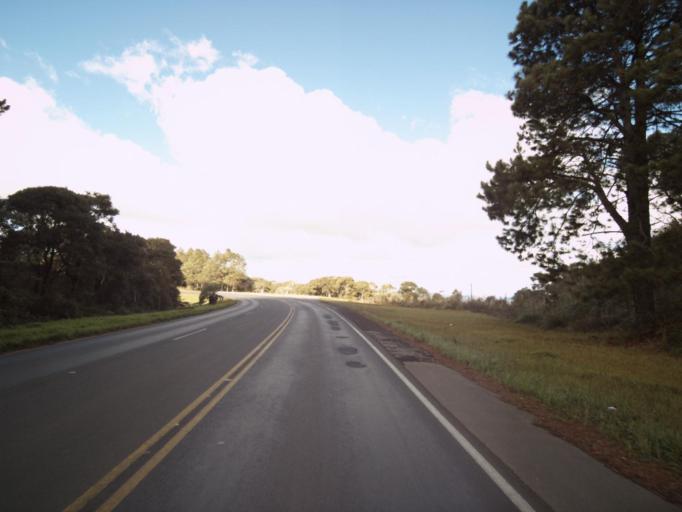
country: BR
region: Santa Catarina
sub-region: Concordia
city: Concordia
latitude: -26.9831
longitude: -51.7928
